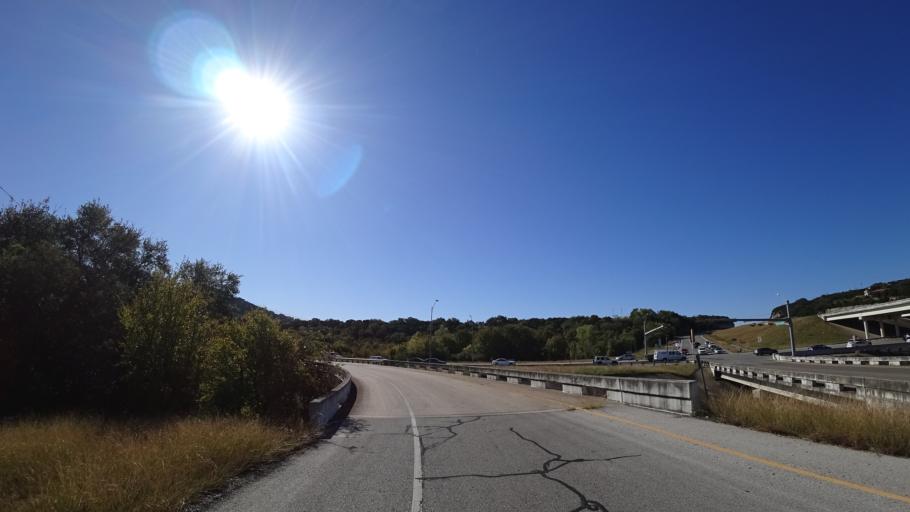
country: US
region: Texas
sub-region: Travis County
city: West Lake Hills
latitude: 30.3600
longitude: -97.7902
